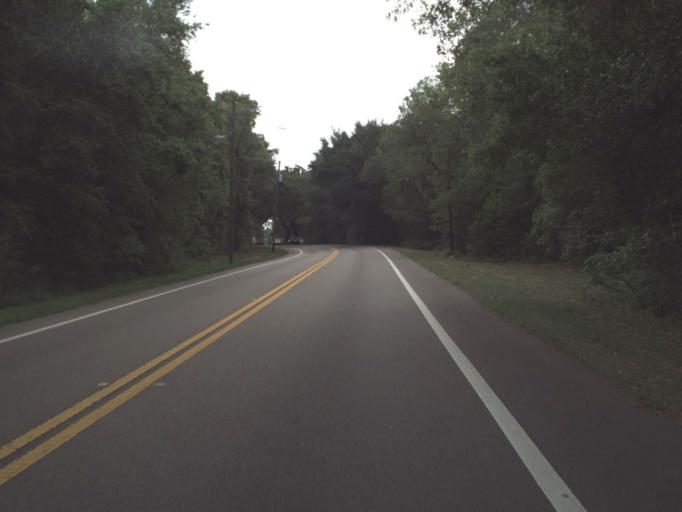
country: US
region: Florida
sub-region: Lake County
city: Umatilla
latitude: 28.9725
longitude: -81.6464
